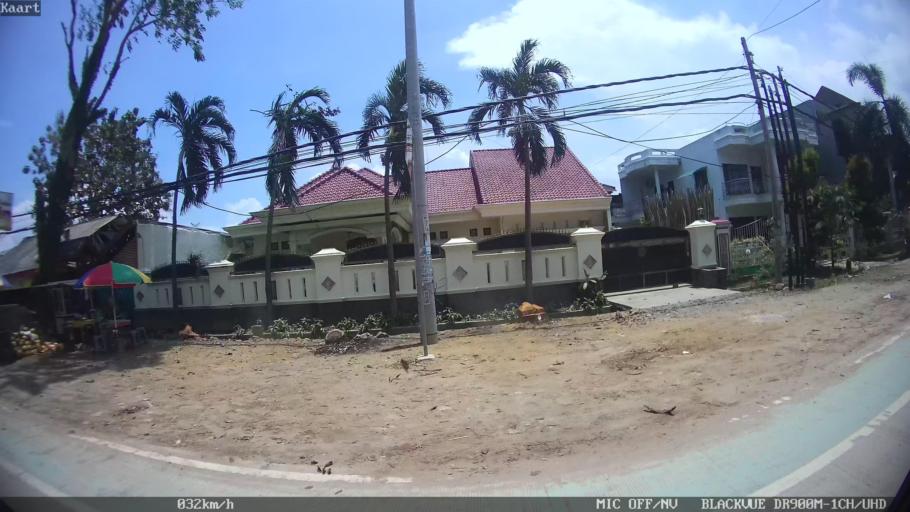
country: ID
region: Lampung
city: Kedaton
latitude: -5.3714
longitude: 105.2977
